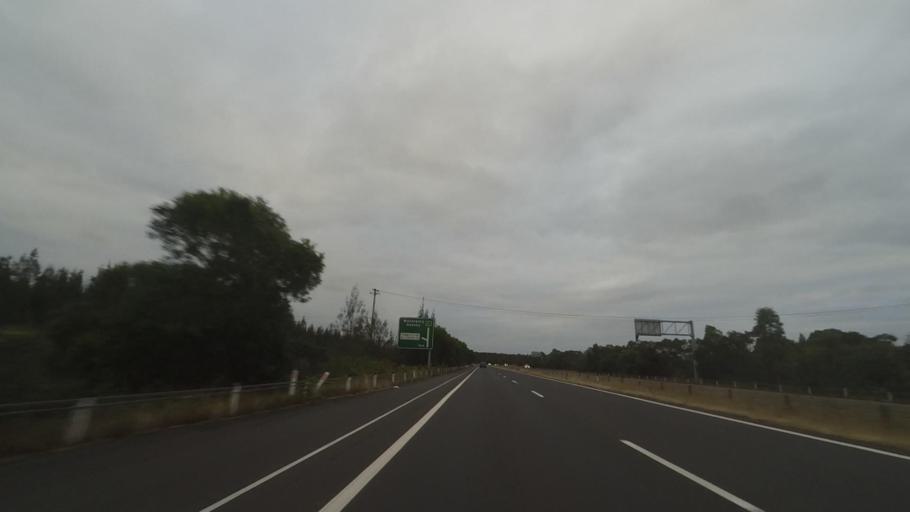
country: AU
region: New South Wales
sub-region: Shellharbour
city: Croom
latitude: -34.6204
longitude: 150.8377
